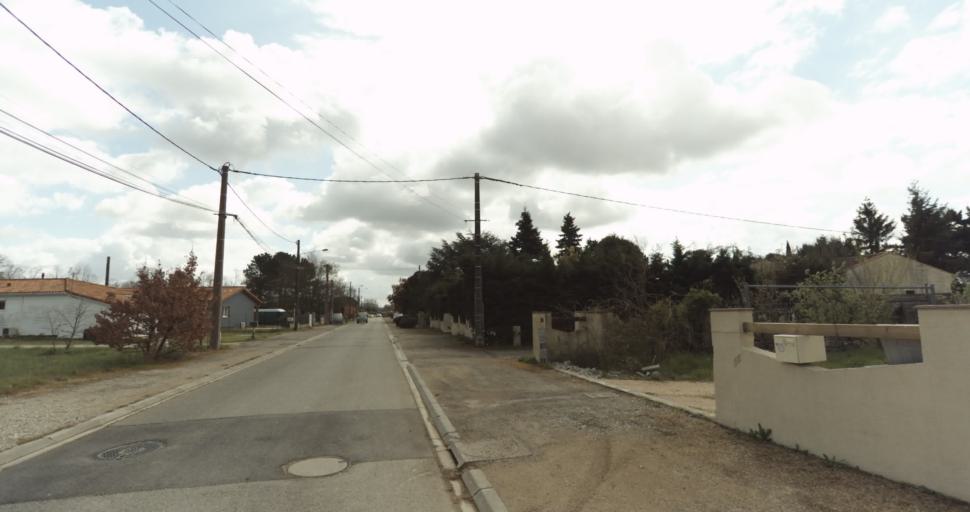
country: FR
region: Midi-Pyrenees
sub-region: Departement de la Haute-Garonne
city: Auterive
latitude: 43.3722
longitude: 1.4568
